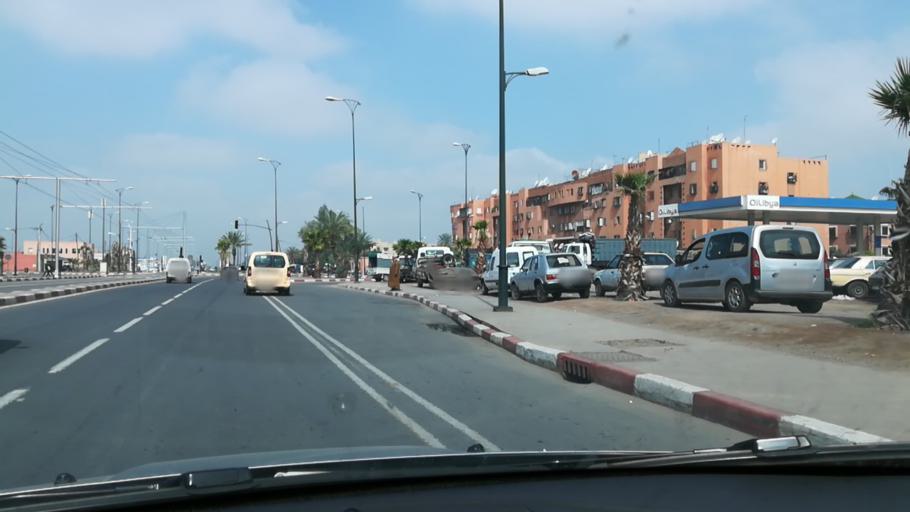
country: MA
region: Marrakech-Tensift-Al Haouz
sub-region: Marrakech
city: Marrakesh
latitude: 31.6280
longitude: -8.0678
